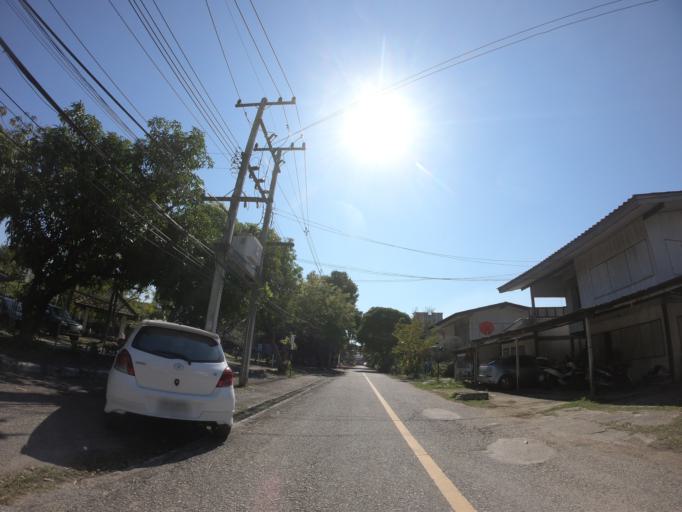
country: TH
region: Chiang Mai
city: Chiang Mai
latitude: 18.7714
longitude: 98.9945
